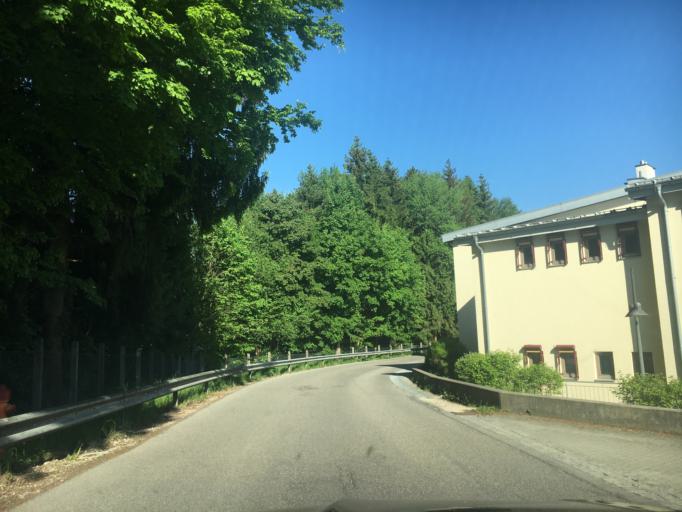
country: DE
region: Bavaria
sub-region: Upper Bavaria
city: Traunreut
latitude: 47.9583
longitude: 12.6137
